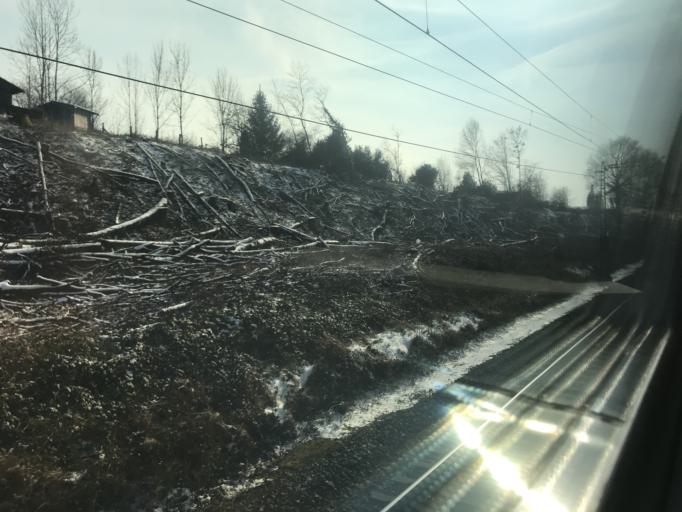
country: DE
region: Rheinland-Pfalz
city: Fohren
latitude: 49.8604
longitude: 6.7681
